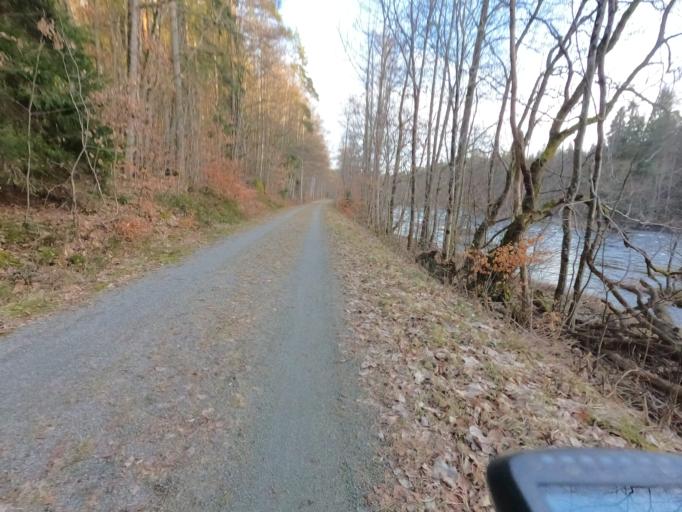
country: SE
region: Blekinge
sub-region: Karlshamns Kommun
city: Svangsta
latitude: 56.3612
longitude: 14.6892
